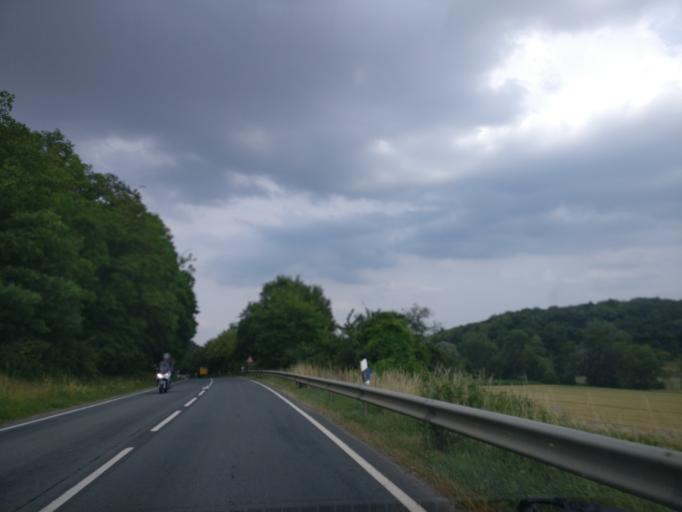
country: DE
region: Lower Saxony
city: Hardegsen
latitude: 51.5864
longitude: 9.8312
